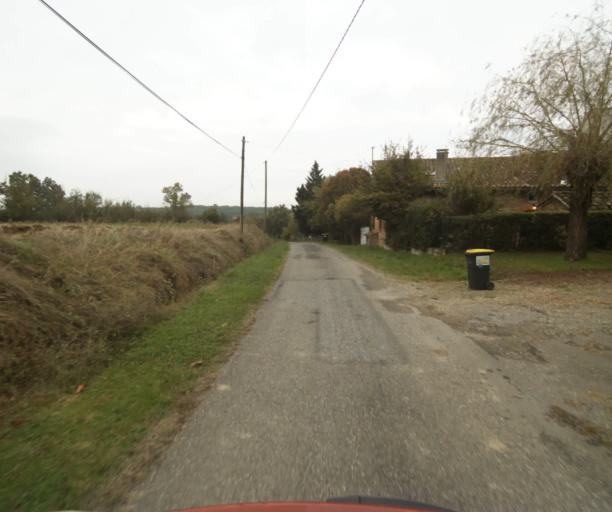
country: FR
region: Midi-Pyrenees
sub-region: Departement de la Haute-Garonne
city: Grenade
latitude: 43.7816
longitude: 1.2287
